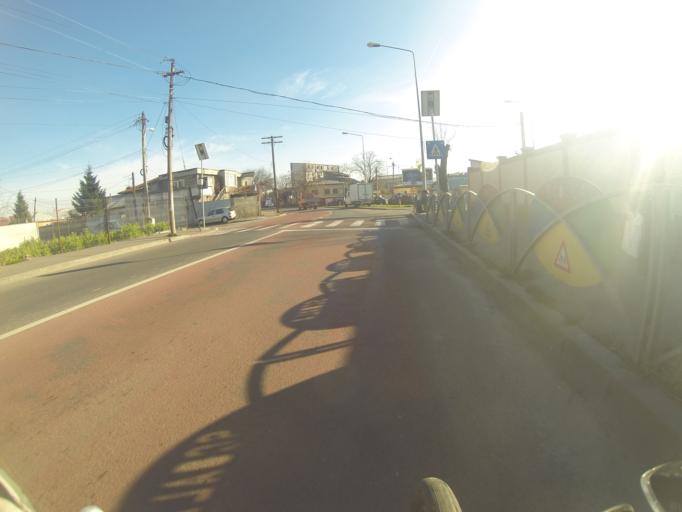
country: RO
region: Bucuresti
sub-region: Municipiul Bucuresti
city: Bucuresti
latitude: 44.3997
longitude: 26.0791
